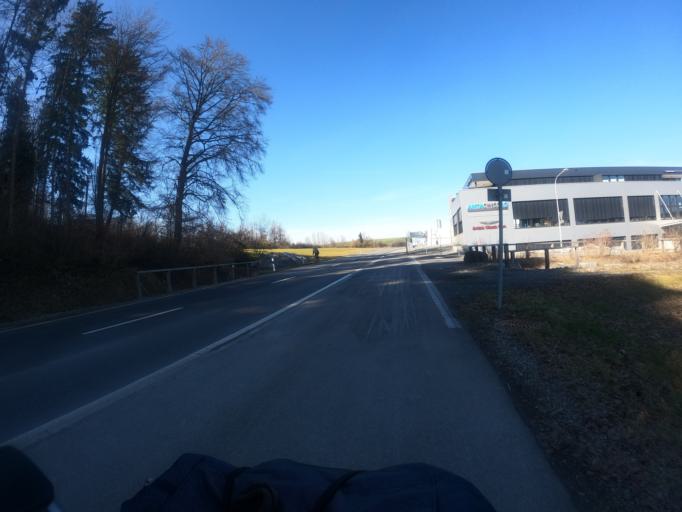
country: CH
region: Zurich
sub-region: Bezirk Affoltern
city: Knonau
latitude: 47.2129
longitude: 8.4686
